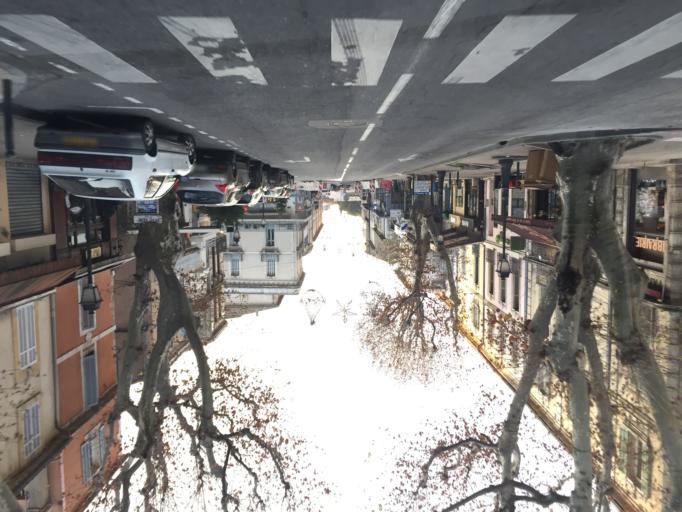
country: FR
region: Provence-Alpes-Cote d'Azur
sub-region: Departement du Vaucluse
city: Cavaillon
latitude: 43.8360
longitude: 5.0407
